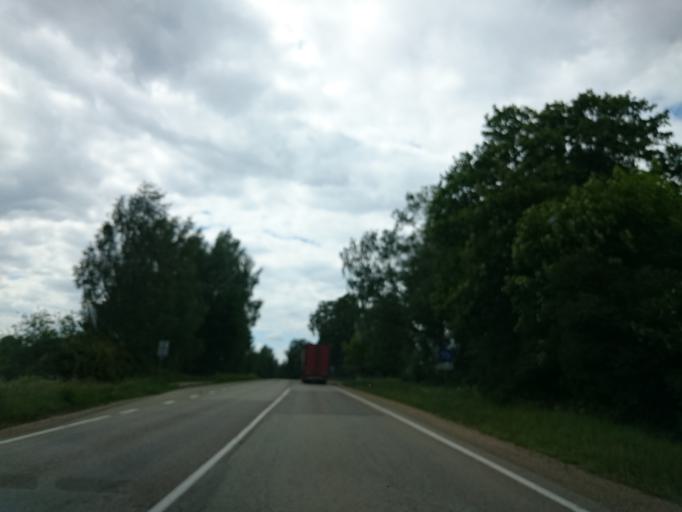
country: LV
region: Ludzas Rajons
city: Ludza
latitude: 56.5342
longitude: 27.5895
